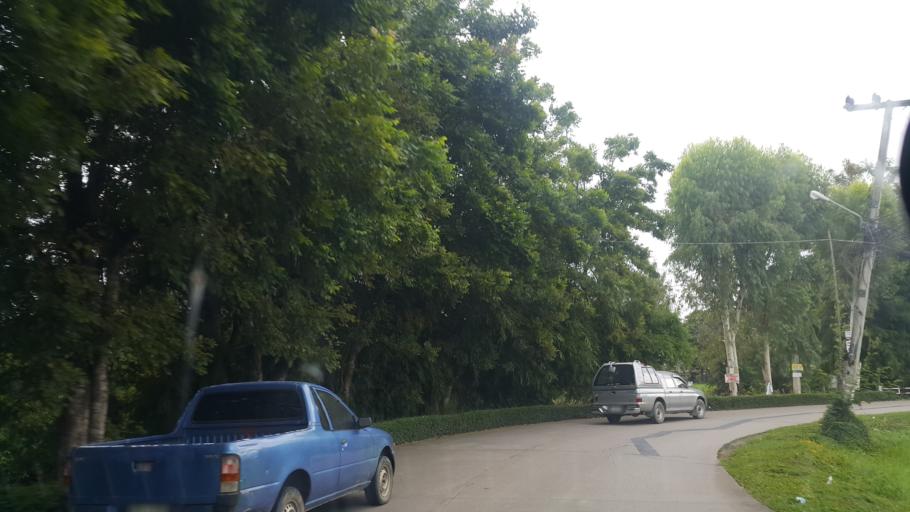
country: TH
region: Chiang Mai
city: San Kamphaeng
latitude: 18.7409
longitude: 99.0767
